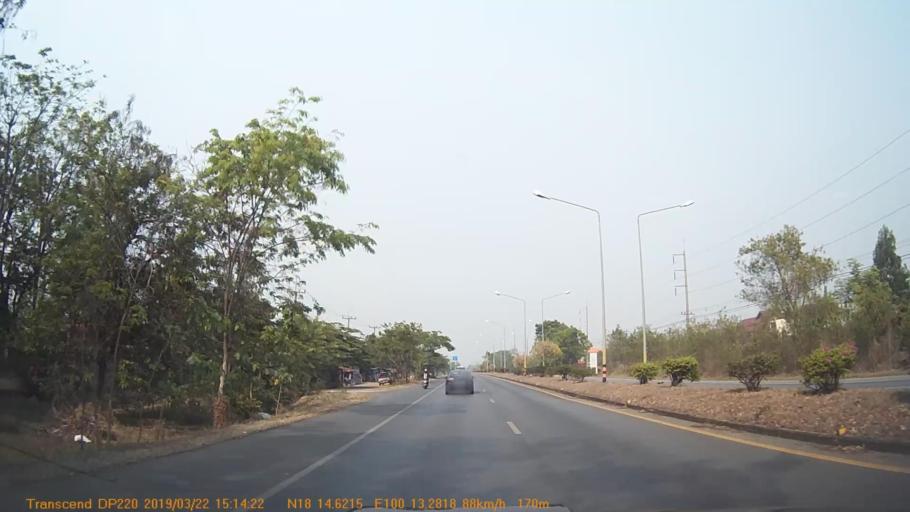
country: TH
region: Phrae
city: Nong Muang Khai
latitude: 18.2440
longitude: 100.2216
